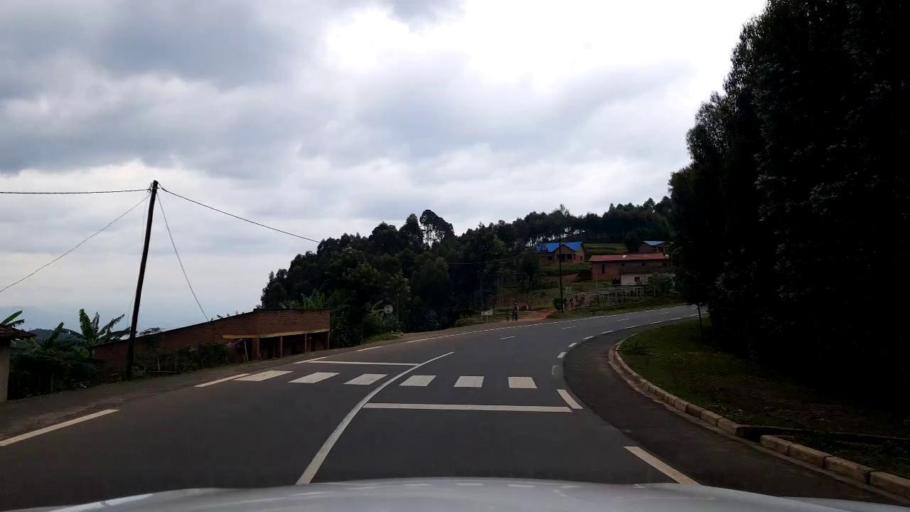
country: RW
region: Western Province
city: Kibuye
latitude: -1.8890
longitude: 29.3455
